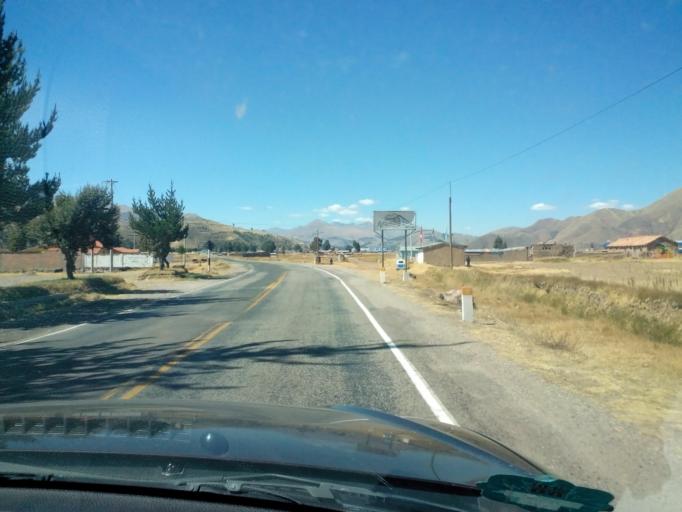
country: PE
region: Cusco
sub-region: Provincia de Canchis
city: San Pablo
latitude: -14.1953
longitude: -71.3277
